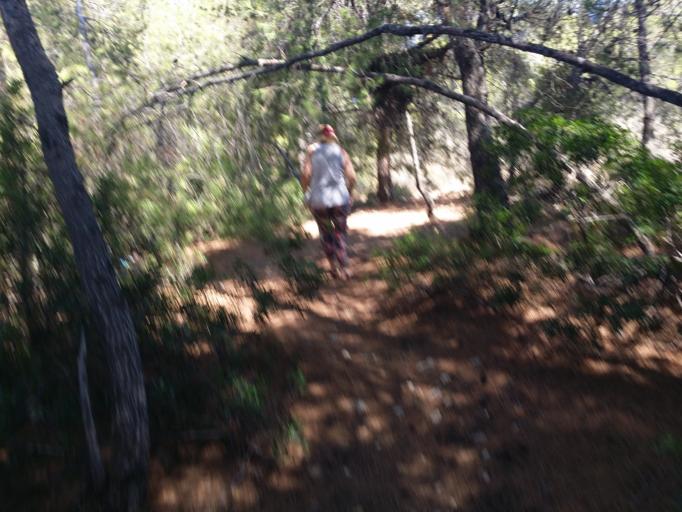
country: GR
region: Attica
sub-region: Nomos Piraios
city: Megalochori
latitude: 37.7017
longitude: 23.3710
